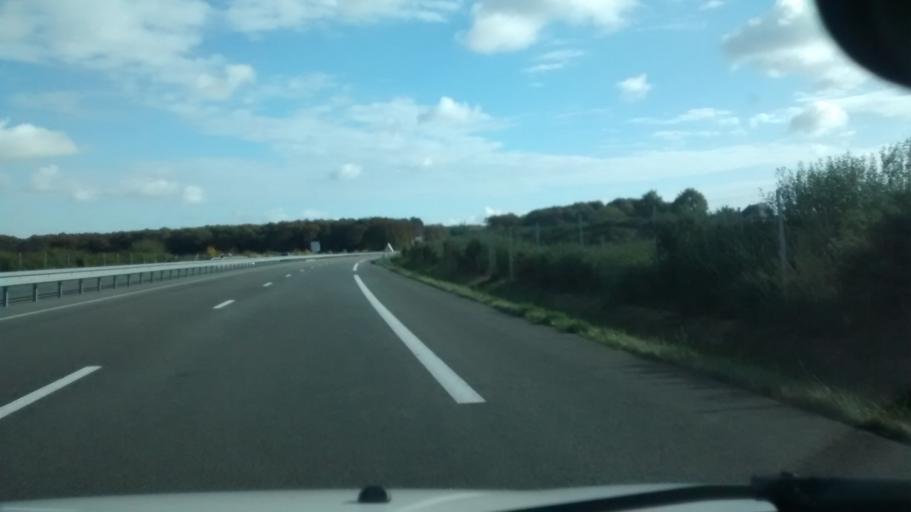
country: FR
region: Pays de la Loire
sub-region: Departement de Maine-et-Loire
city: Combree
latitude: 47.7311
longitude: -1.0772
